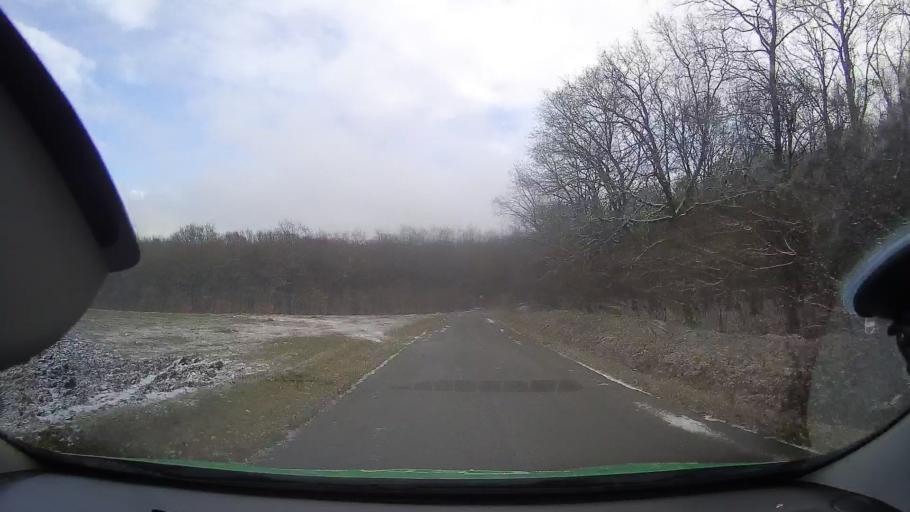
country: RO
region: Mures
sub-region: Comuna Ludus
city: Gheja
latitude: 46.4012
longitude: 24.0165
